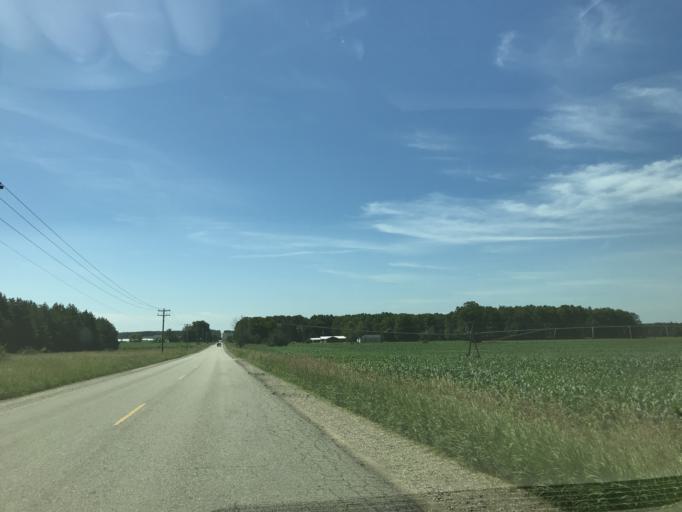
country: US
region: Michigan
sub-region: Missaukee County
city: Lake City
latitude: 44.3290
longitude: -85.0751
